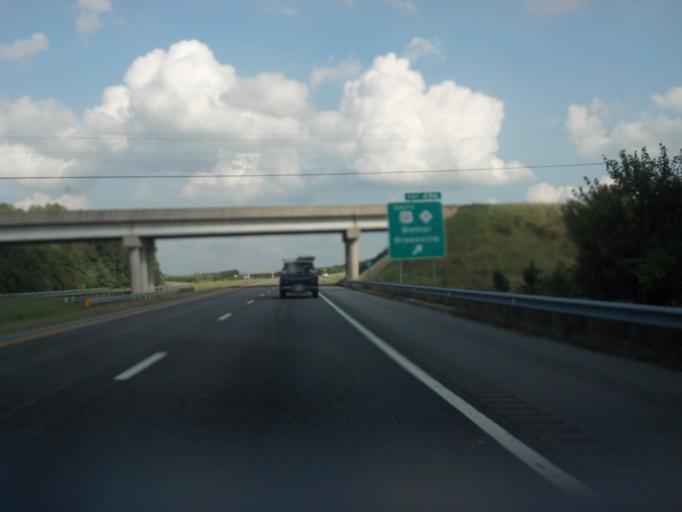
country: US
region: North Carolina
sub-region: Pitt County
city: Bethel
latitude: 35.8364
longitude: -77.3812
